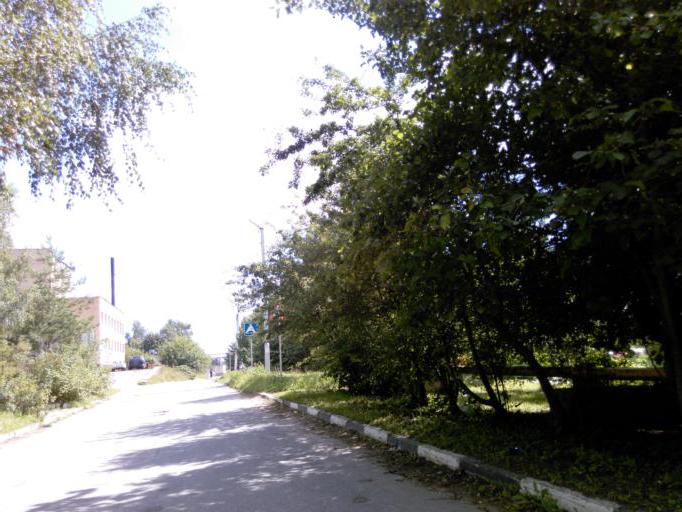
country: RU
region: Moskovskaya
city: Solnechnogorsk
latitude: 56.1422
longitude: 36.8932
